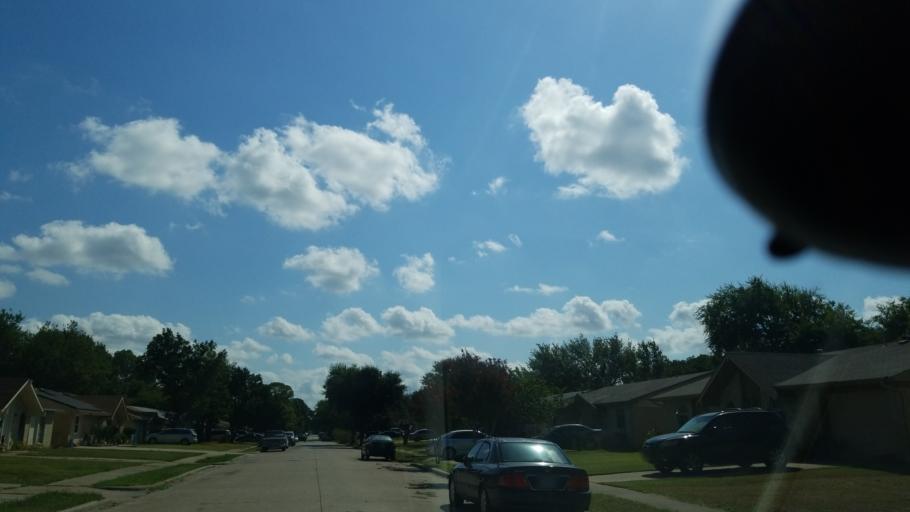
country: US
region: Texas
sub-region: Dallas County
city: Grand Prairie
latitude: 32.7047
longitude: -96.9932
